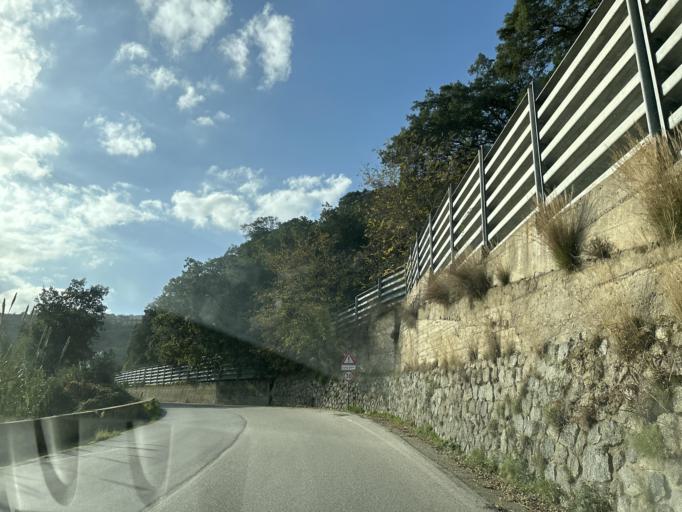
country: IT
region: Calabria
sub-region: Provincia di Catanzaro
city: Gasperina
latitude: 38.7273
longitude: 16.5118
